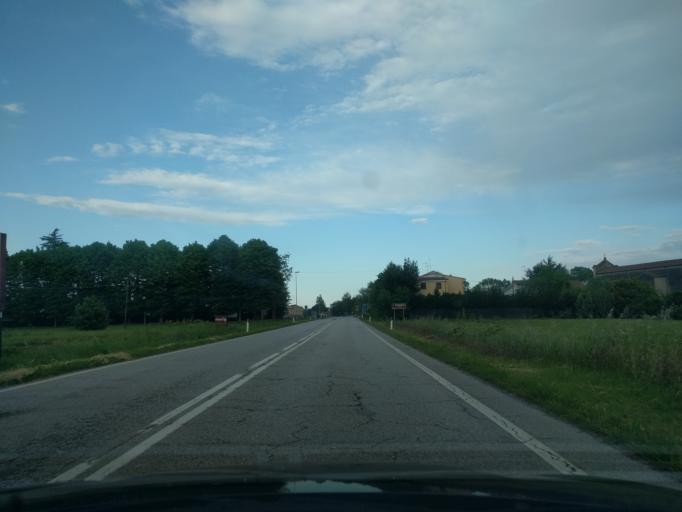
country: IT
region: Emilia-Romagna
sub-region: Provincia di Ferrara
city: Ro
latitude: 44.9312
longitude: 11.7194
